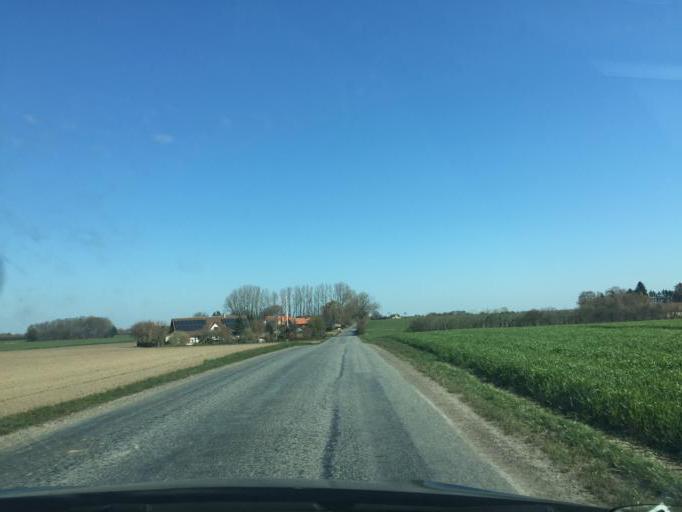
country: DK
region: South Denmark
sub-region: Faaborg-Midtfyn Kommune
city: Ringe
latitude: 55.2675
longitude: 10.5267
